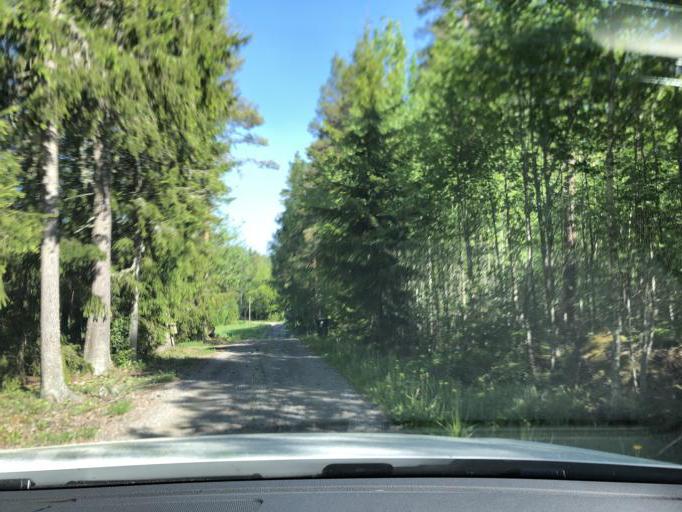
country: SE
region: Dalarna
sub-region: Avesta Kommun
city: Horndal
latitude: 60.2042
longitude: 16.4969
